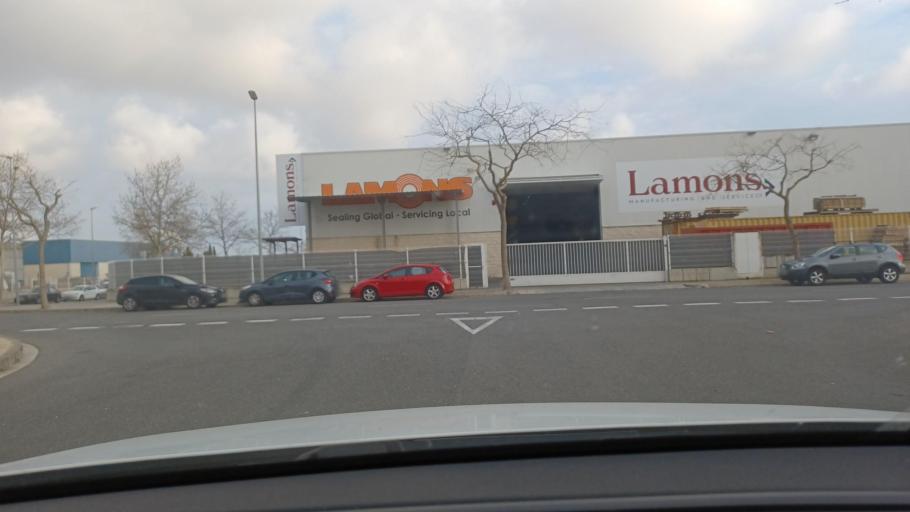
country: ES
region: Catalonia
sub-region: Provincia de Tarragona
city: Vila-seca
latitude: 41.1192
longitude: 1.1493
